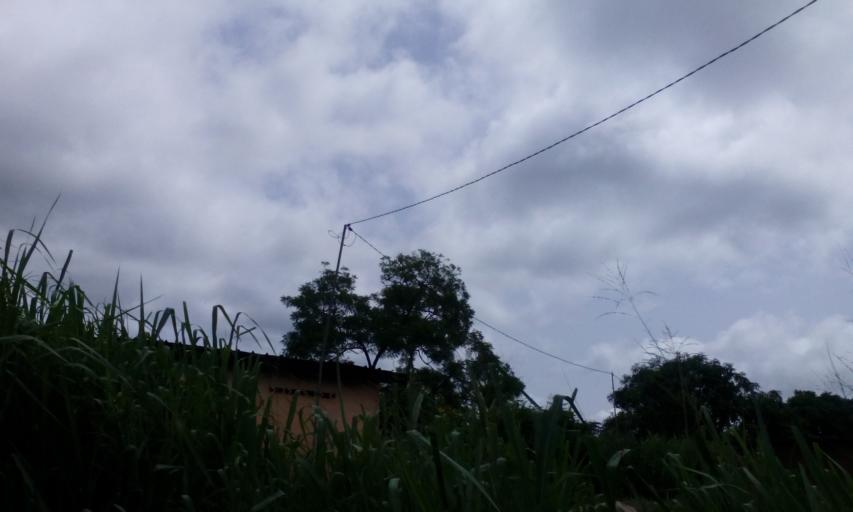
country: CI
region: Dix-Huit Montagnes
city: Man
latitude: 7.2883
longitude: -7.3887
